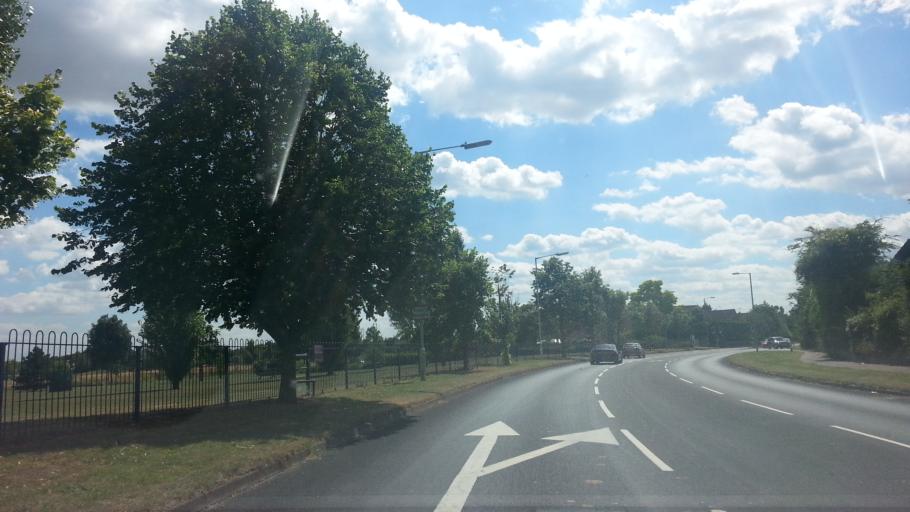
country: GB
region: England
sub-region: Essex
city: Chelmsford
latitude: 51.7364
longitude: 0.5114
